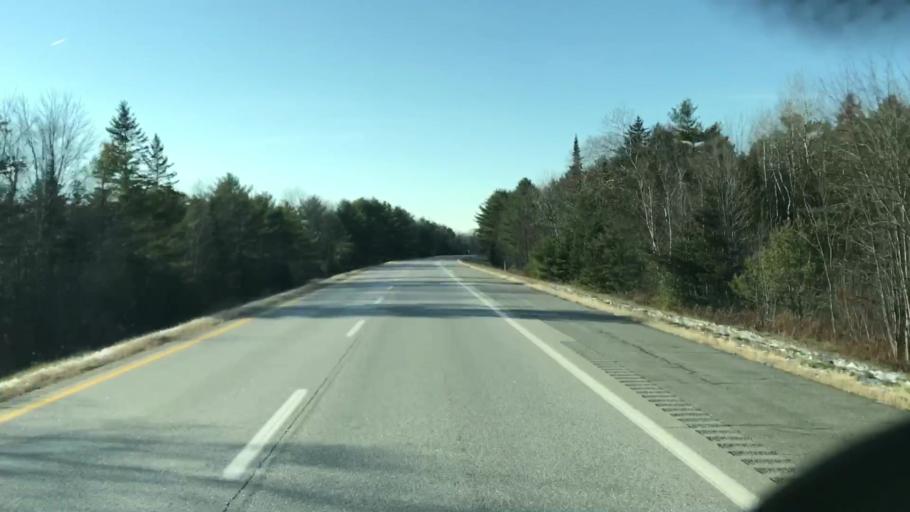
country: US
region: Maine
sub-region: Penobscot County
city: Carmel
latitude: 44.7741
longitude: -69.0266
